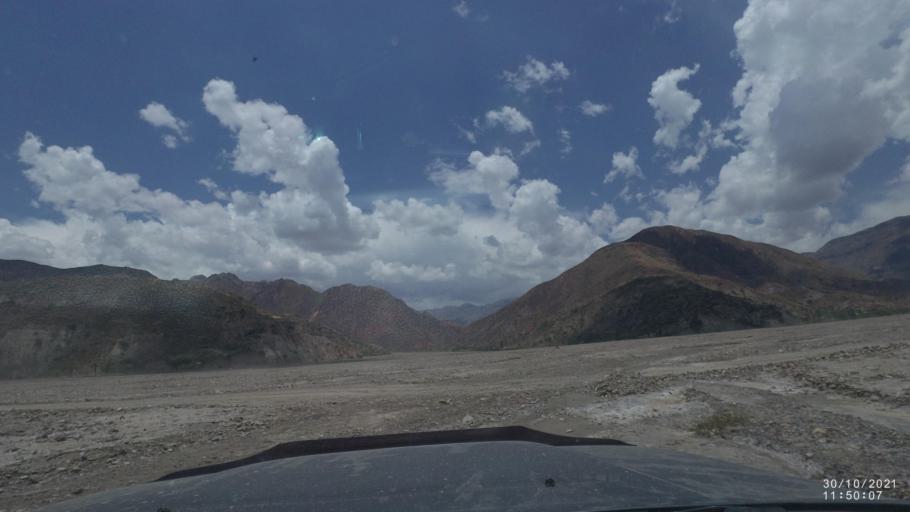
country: BO
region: Cochabamba
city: Colchani
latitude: -17.5181
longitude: -66.6181
